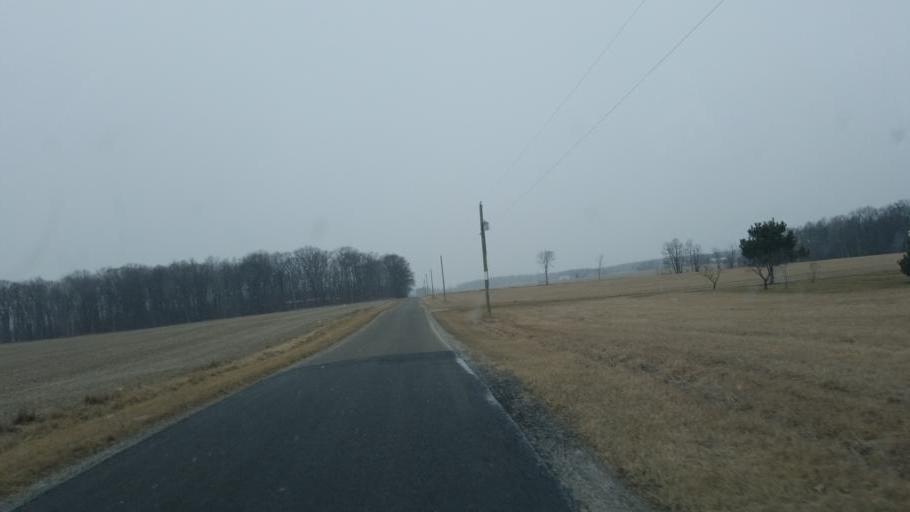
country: US
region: Ohio
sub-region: Defiance County
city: Hicksville
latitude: 41.3393
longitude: -84.7348
